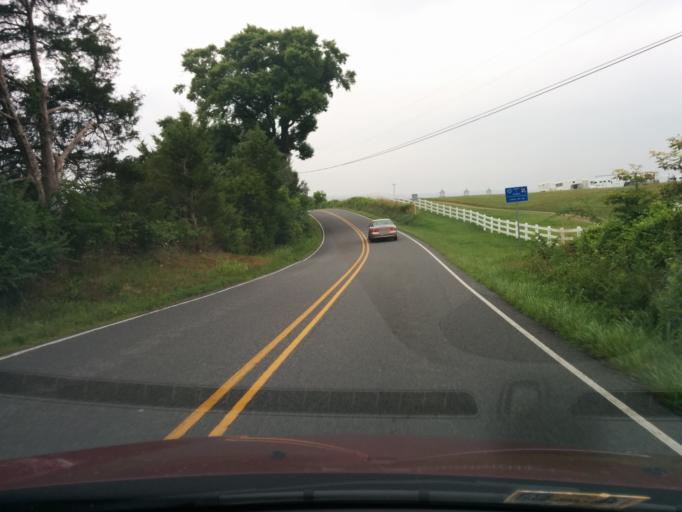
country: US
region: Virginia
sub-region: Rockbridge County
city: East Lexington
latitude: 37.8142
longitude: -79.4246
